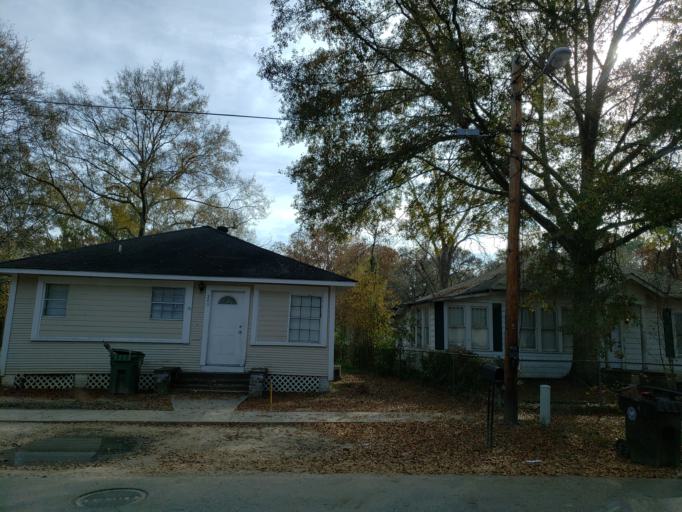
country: US
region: Mississippi
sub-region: Forrest County
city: Hattiesburg
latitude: 31.3340
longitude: -89.3010
